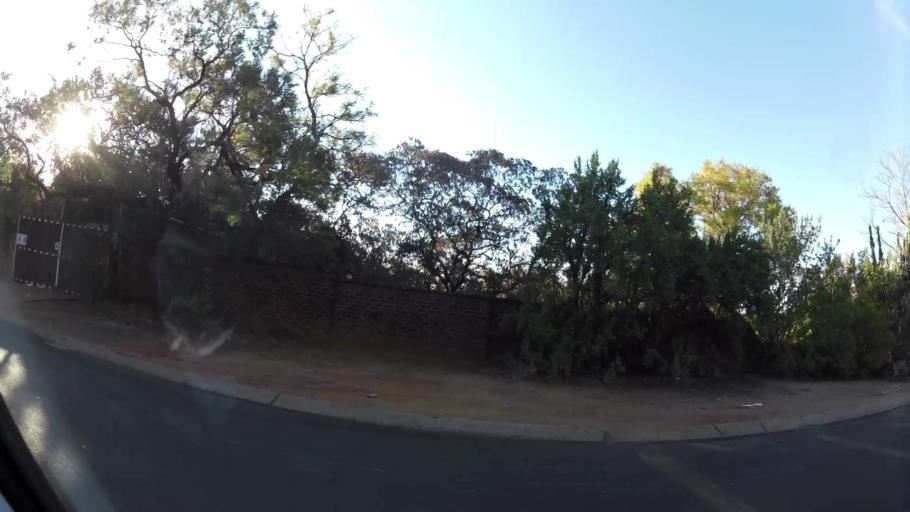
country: ZA
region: North-West
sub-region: Bojanala Platinum District Municipality
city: Rustenburg
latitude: -25.6892
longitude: 27.2075
